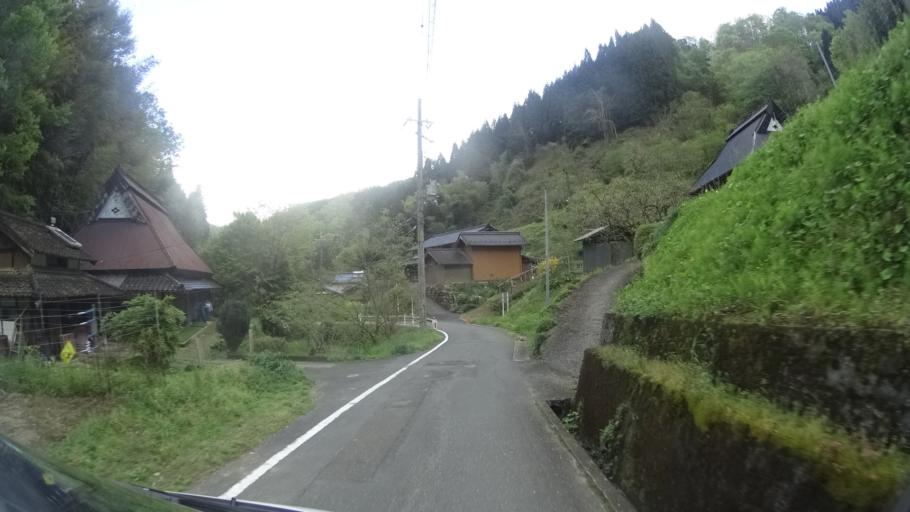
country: JP
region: Kyoto
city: Ayabe
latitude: 35.2566
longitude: 135.3365
